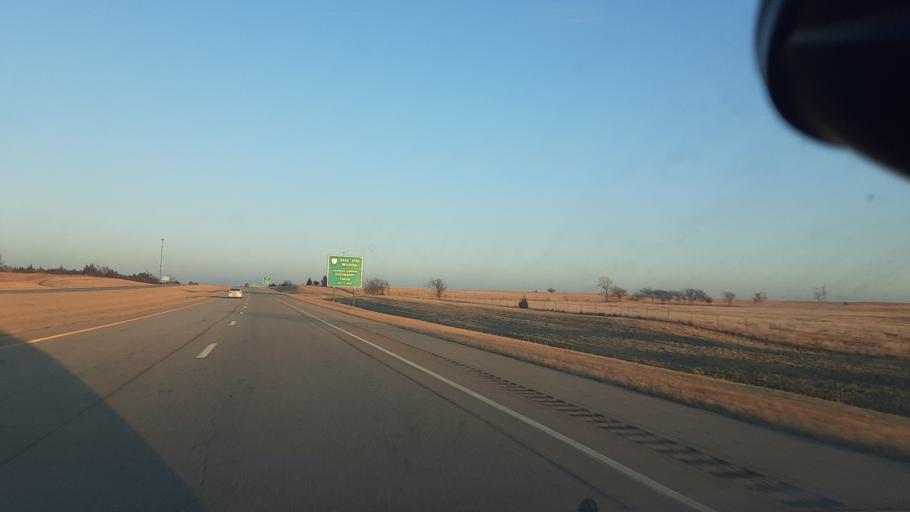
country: US
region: Oklahoma
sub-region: Noble County
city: Perry
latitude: 36.3983
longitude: -97.3520
